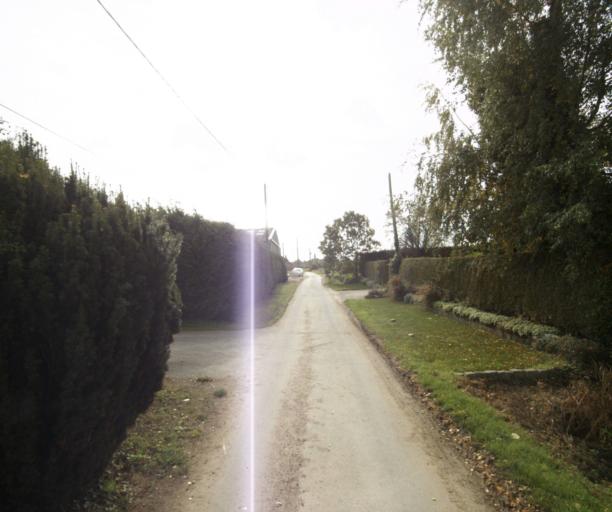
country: FR
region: Nord-Pas-de-Calais
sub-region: Departement du Nord
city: Bois-Grenier
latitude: 50.6233
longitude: 2.8811
